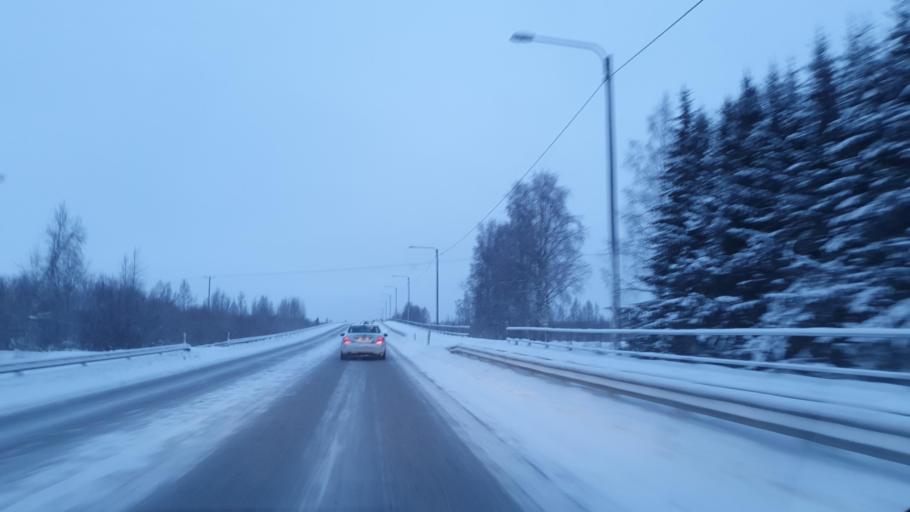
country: FI
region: Northern Ostrobothnia
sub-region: Oulu
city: Muhos
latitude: 64.8014
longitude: 26.0417
